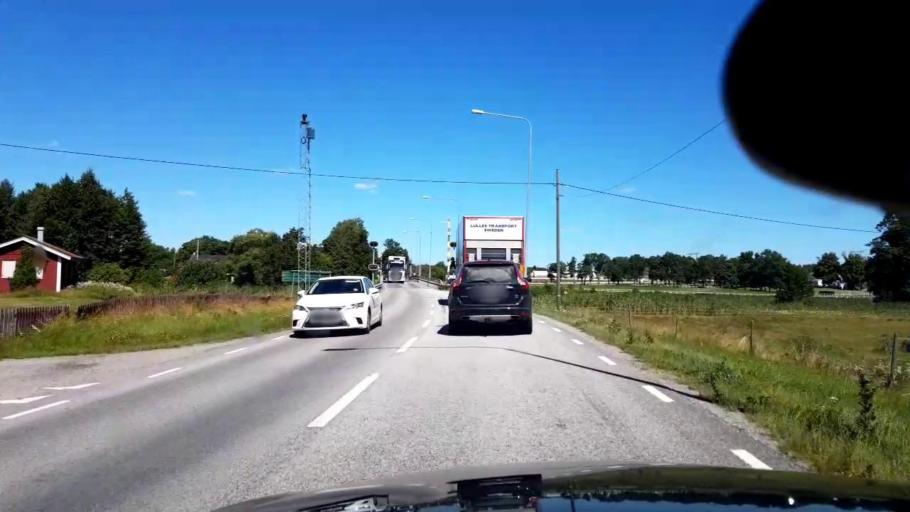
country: SE
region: Uppsala
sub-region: Habo Kommun
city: Balsta
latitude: 59.6392
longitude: 17.6093
